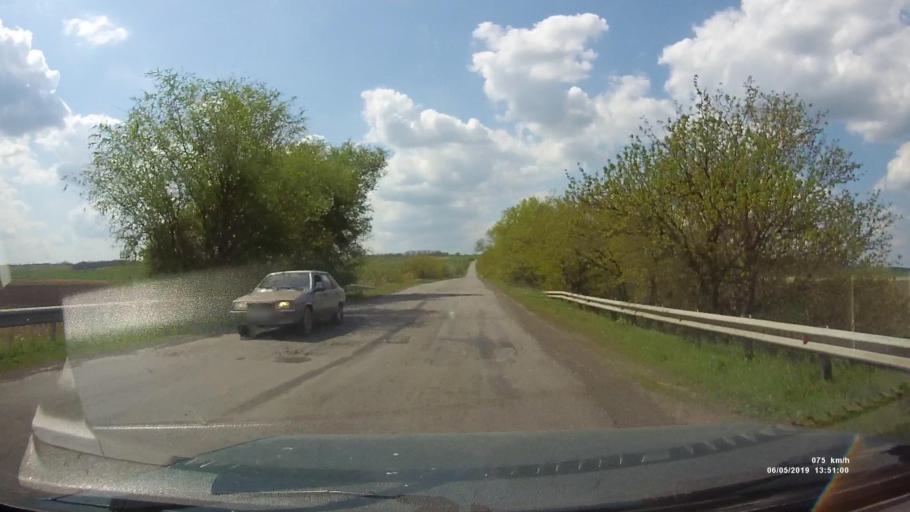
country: RU
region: Rostov
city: Melikhovskaya
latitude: 47.6554
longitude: 40.4987
